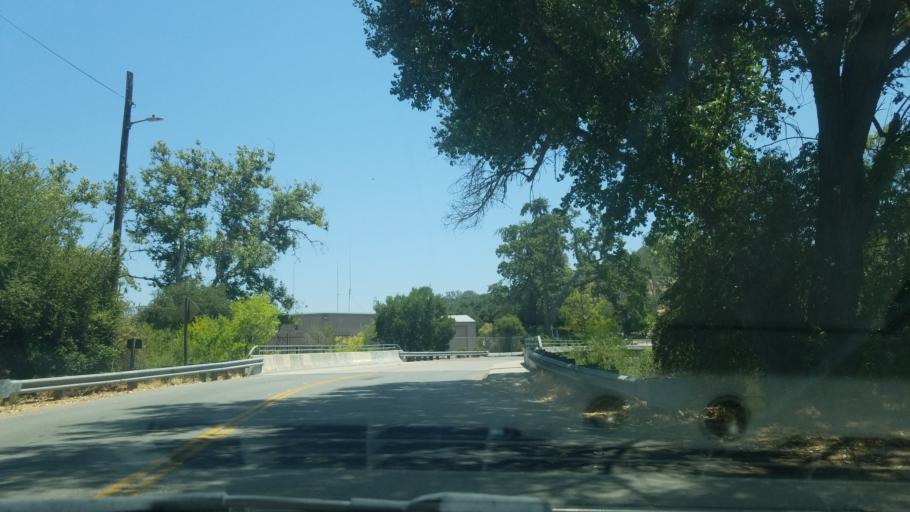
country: US
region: California
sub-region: San Luis Obispo County
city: Atascadero
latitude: 35.5020
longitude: -120.6627
